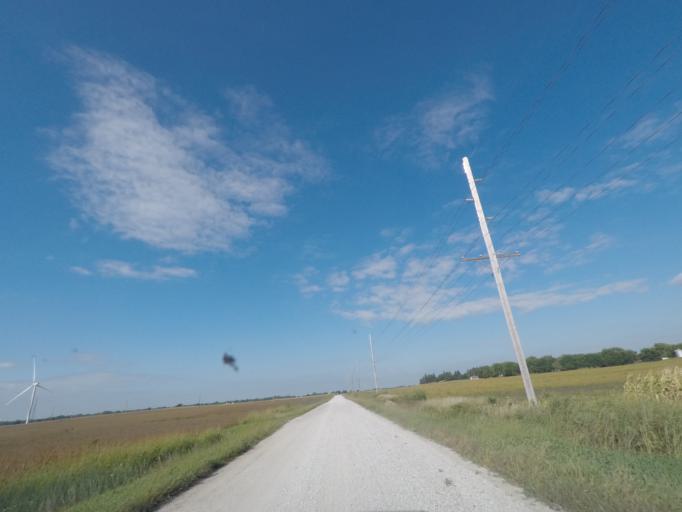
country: US
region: Iowa
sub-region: Story County
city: Nevada
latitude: 42.0347
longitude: -93.4200
